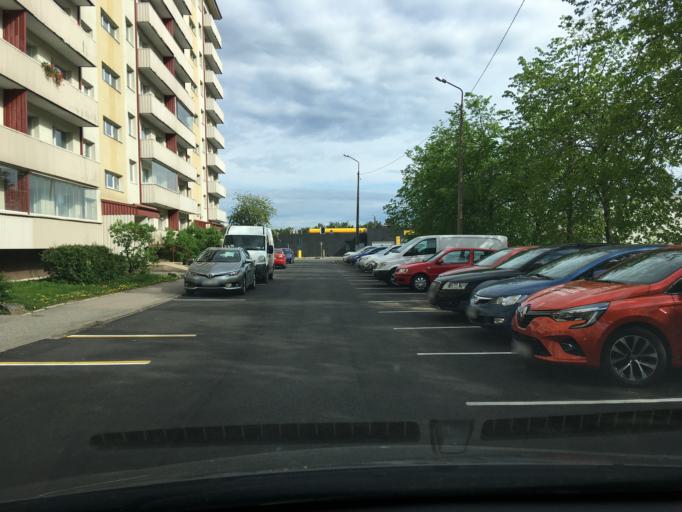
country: EE
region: Harju
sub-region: Saue vald
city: Laagri
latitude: 59.3968
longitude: 24.6774
